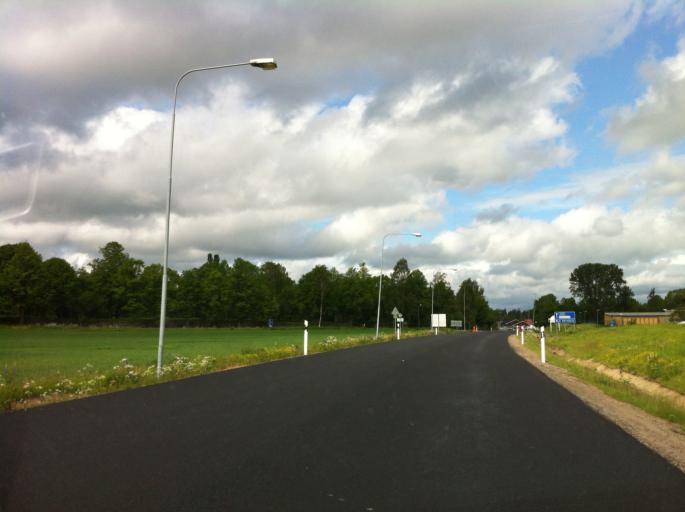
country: SE
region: Vaermland
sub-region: Sunne Kommun
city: Sunne
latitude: 59.8389
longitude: 13.1624
